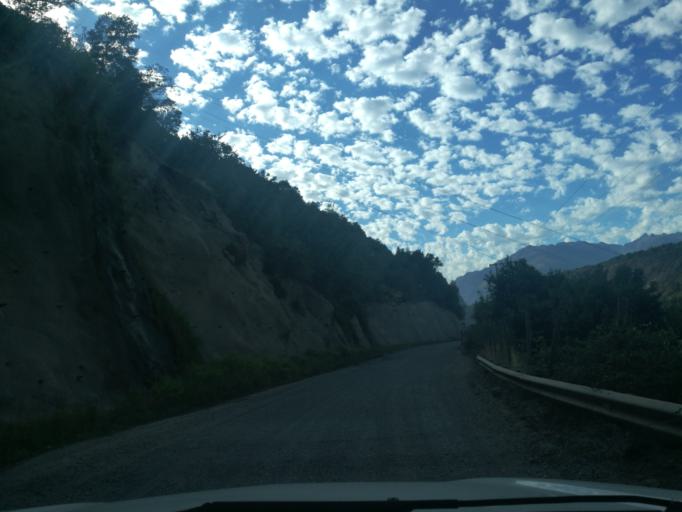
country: CL
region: O'Higgins
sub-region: Provincia de Cachapoal
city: Machali
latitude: -34.2748
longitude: -70.4516
